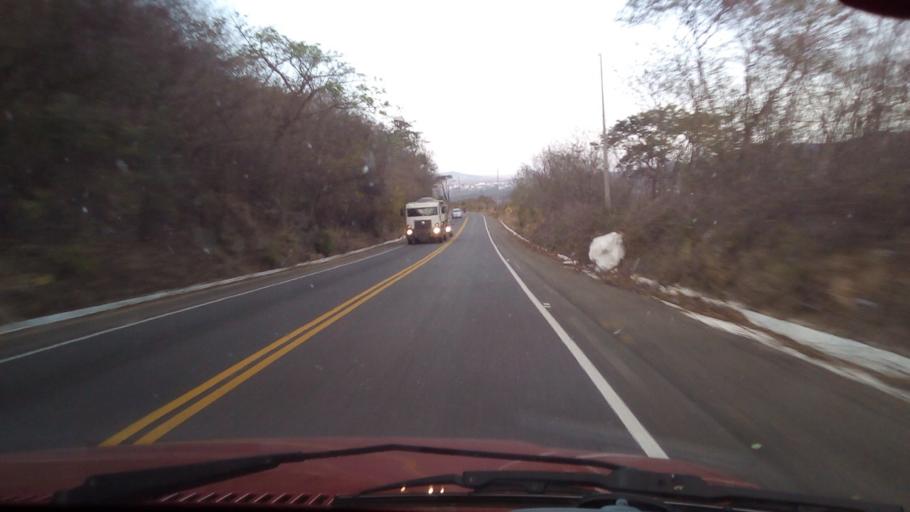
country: BR
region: Paraiba
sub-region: Bananeiras
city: Solanea
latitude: -6.7337
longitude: -35.5558
